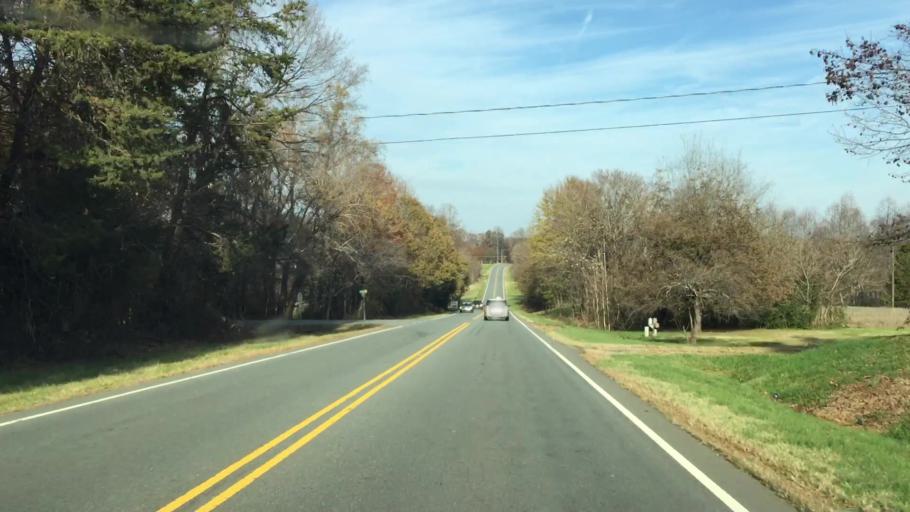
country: US
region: North Carolina
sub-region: Forsyth County
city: Walkertown
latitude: 36.1790
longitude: -80.1219
